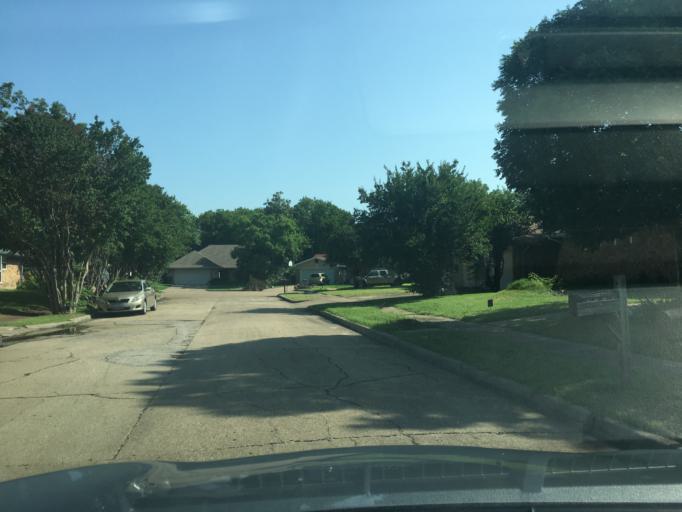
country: US
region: Texas
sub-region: Dallas County
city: Richardson
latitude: 32.9289
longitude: -96.6880
